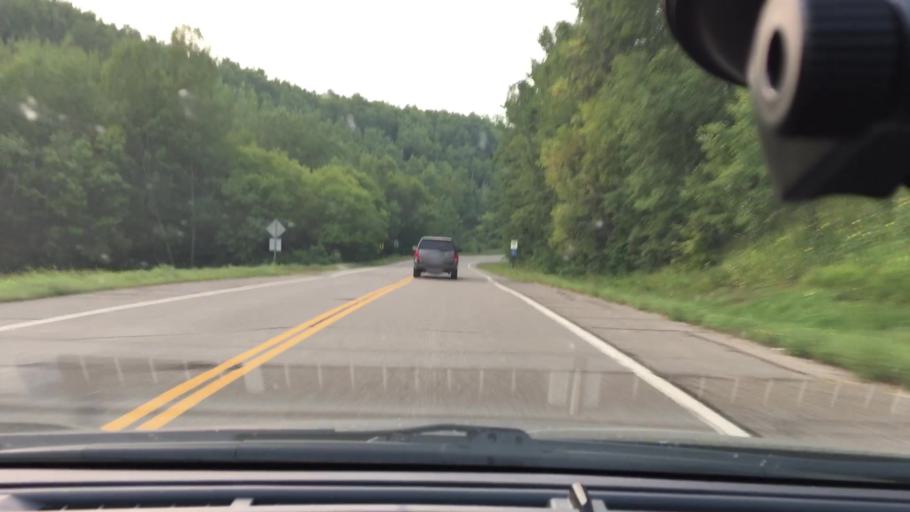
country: US
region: Minnesota
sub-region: Crow Wing County
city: Crosby
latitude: 46.5193
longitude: -93.9236
